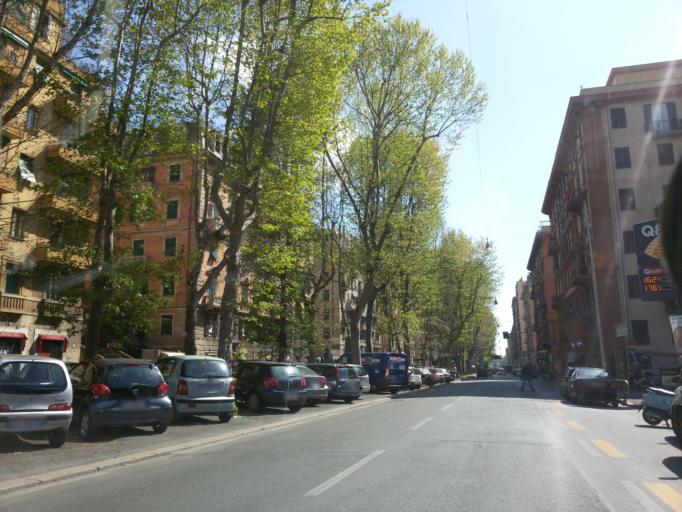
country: IT
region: Liguria
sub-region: Provincia di Genova
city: Genoa
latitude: 44.4143
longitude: 8.9561
